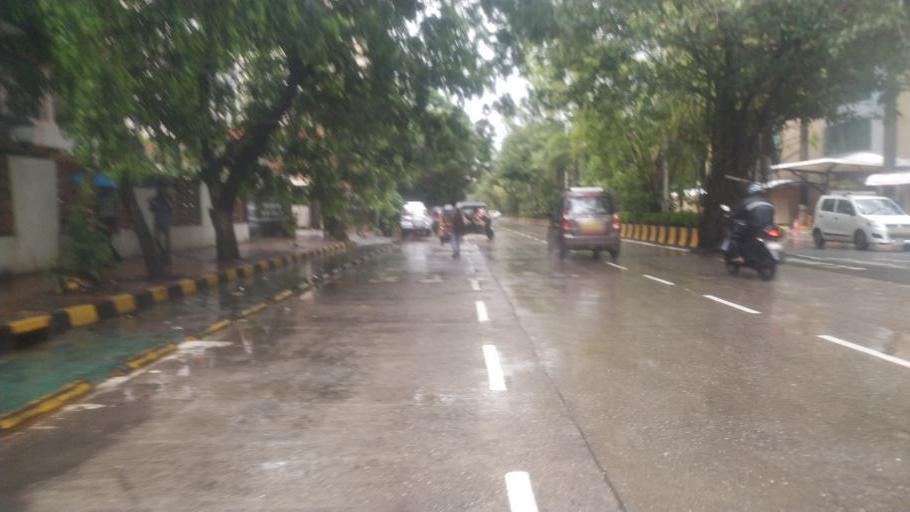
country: IN
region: Maharashtra
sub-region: Mumbai Suburban
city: Mumbai
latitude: 19.0675
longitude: 72.8700
